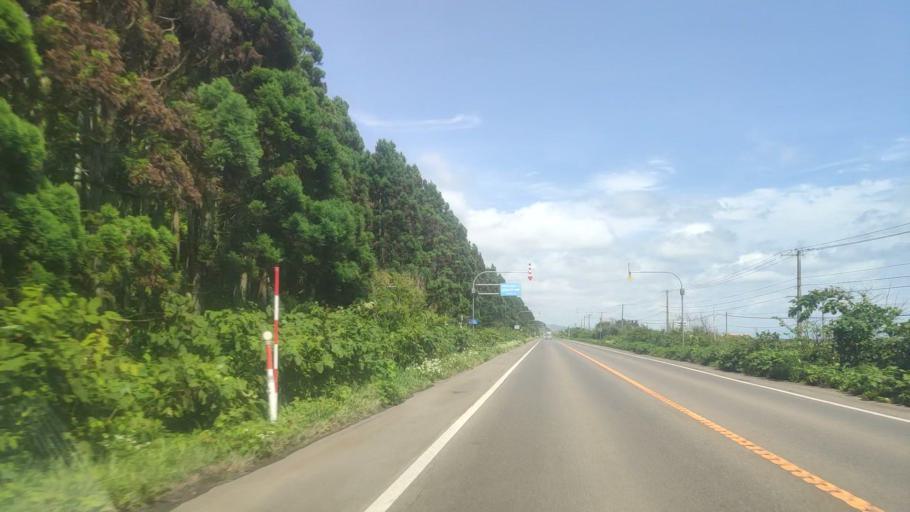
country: JP
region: Hokkaido
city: Niseko Town
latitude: 42.3388
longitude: 140.2802
